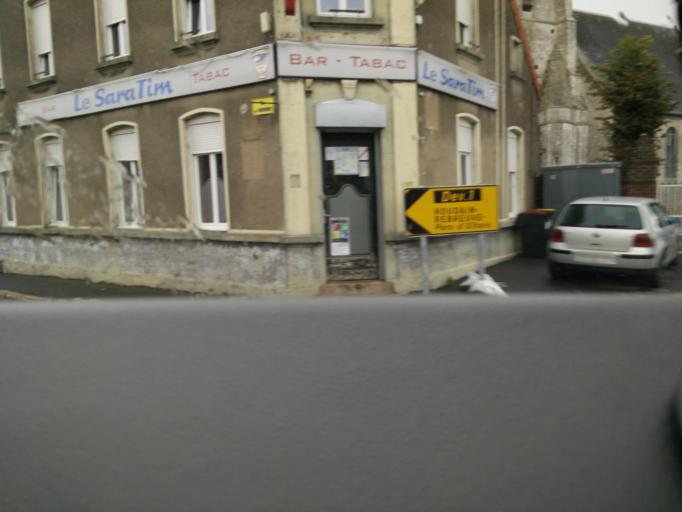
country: FR
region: Nord-Pas-de-Calais
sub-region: Departement du Pas-de-Calais
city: Bouvigny-Boyeffles
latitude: 50.4100
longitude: 2.6423
